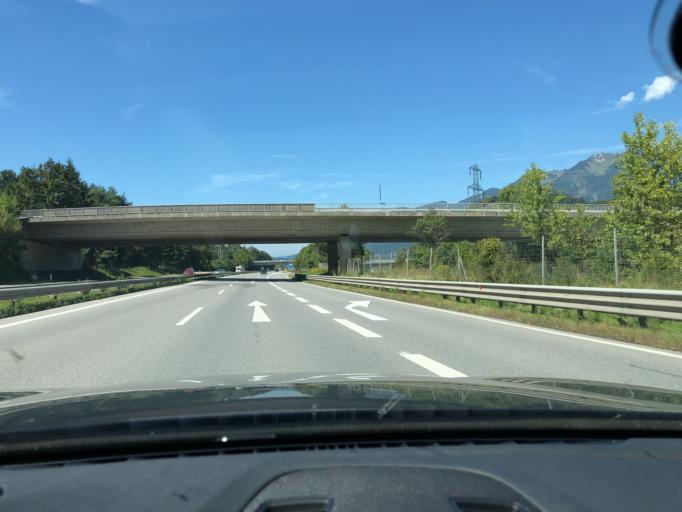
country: AT
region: Vorarlberg
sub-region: Politischer Bezirk Bludenz
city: Nuziders
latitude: 47.1651
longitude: 9.7928
